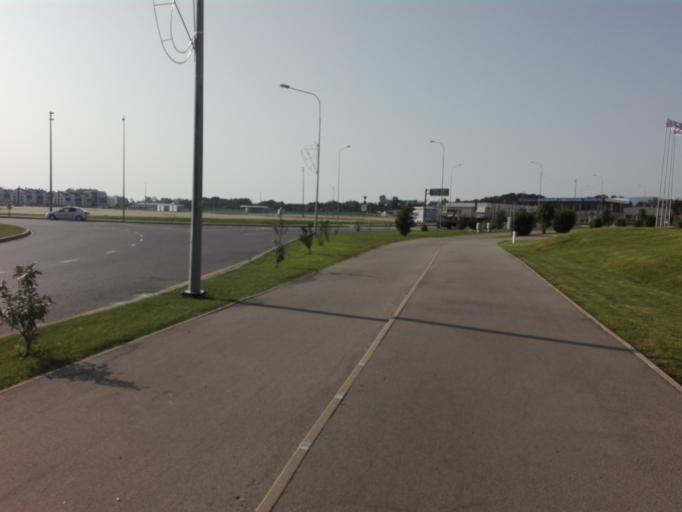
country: RU
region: Krasnodarskiy
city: Adler
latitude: 43.4114
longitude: 39.9497
